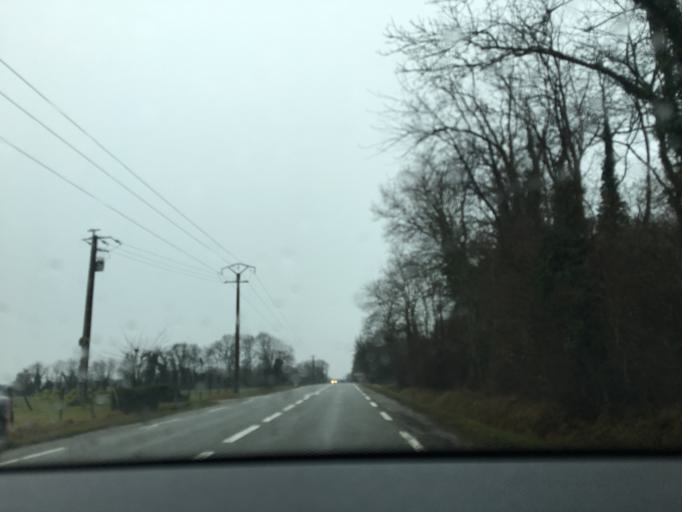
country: FR
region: Ile-de-France
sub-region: Departement des Yvelines
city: Limay
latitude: 49.0218
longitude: 1.7403
